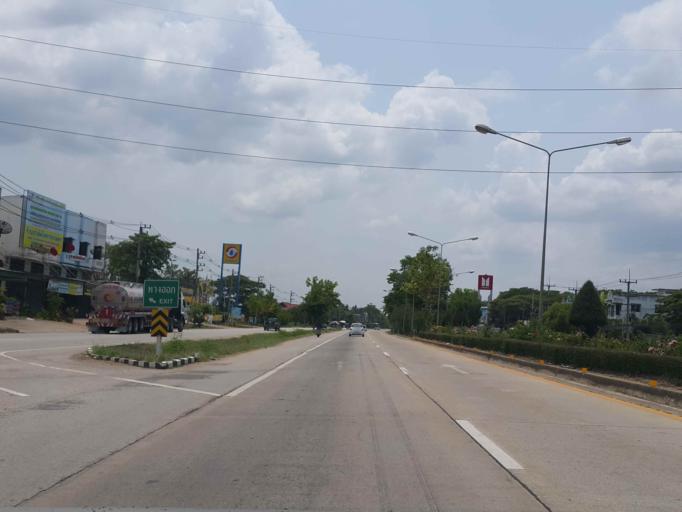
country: TH
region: Lampang
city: Lampang
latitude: 18.2490
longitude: 99.4516
